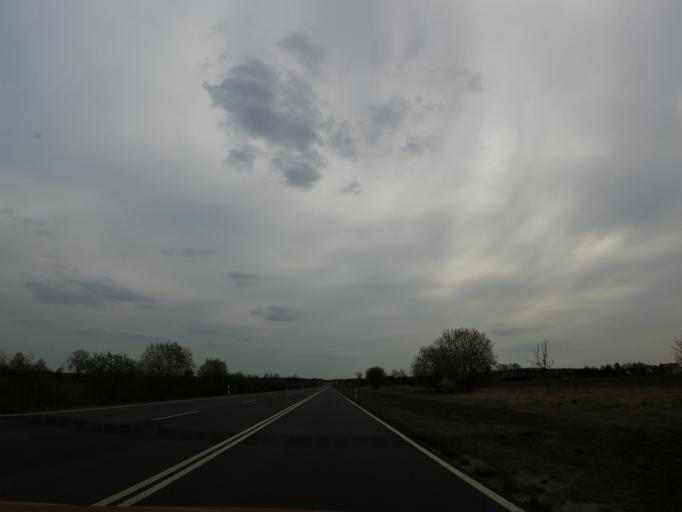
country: DE
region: Brandenburg
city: Beeskow
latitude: 52.1756
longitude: 14.2168
